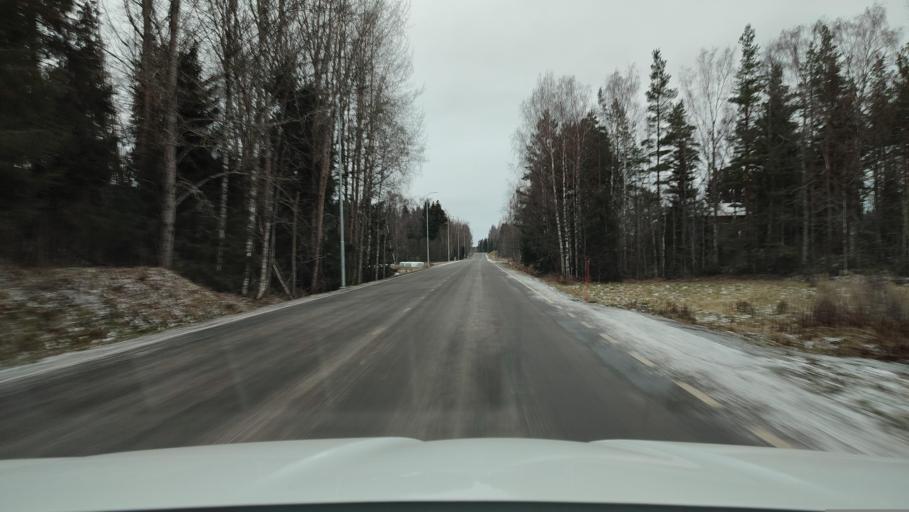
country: FI
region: Ostrobothnia
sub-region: Vaasa
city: Ristinummi
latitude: 63.0413
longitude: 21.7791
